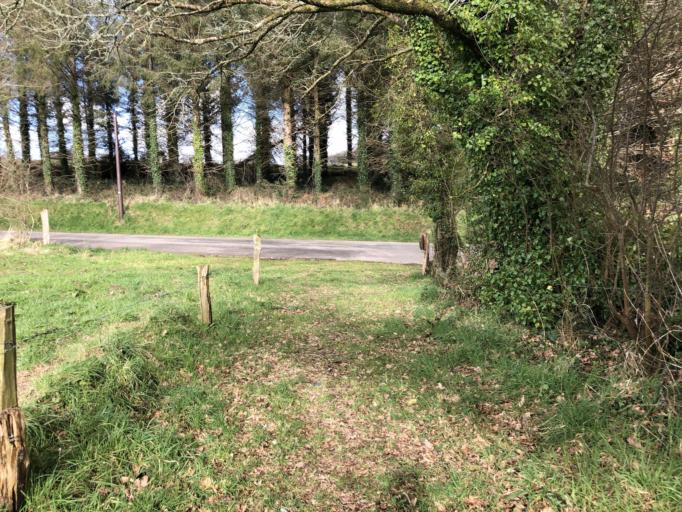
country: FR
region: Brittany
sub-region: Departement du Finistere
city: Sizun
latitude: 48.4029
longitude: -3.9836
